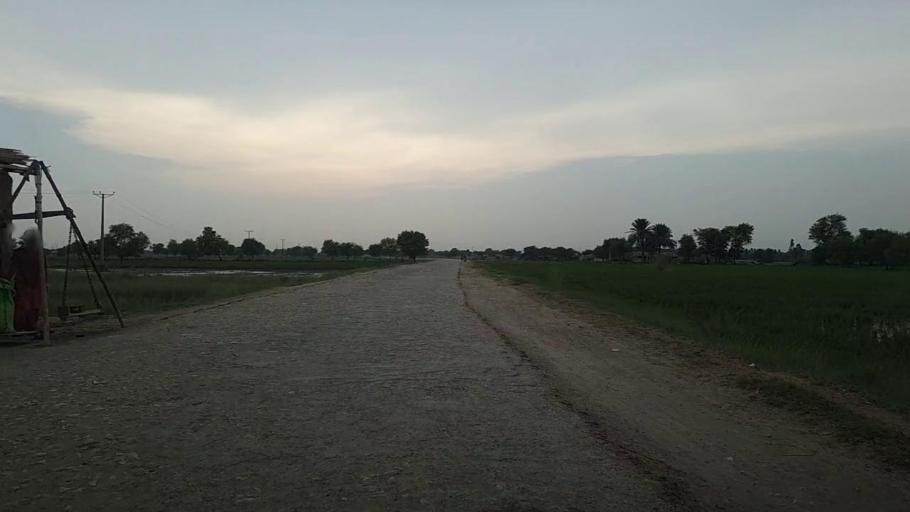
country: PK
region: Sindh
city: Khanpur
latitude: 27.8484
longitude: 69.4452
